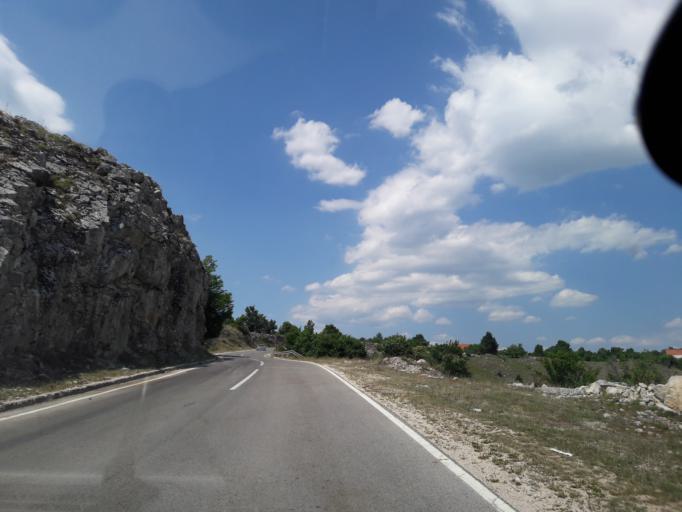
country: BA
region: Republika Srpska
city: Sipovo
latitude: 44.1653
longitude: 17.1686
